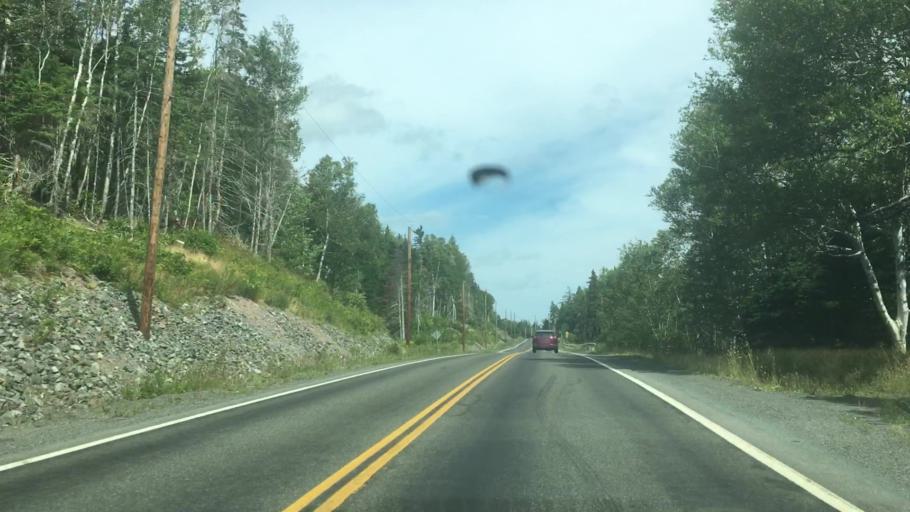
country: CA
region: Nova Scotia
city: Sydney Mines
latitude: 46.2094
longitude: -60.6220
